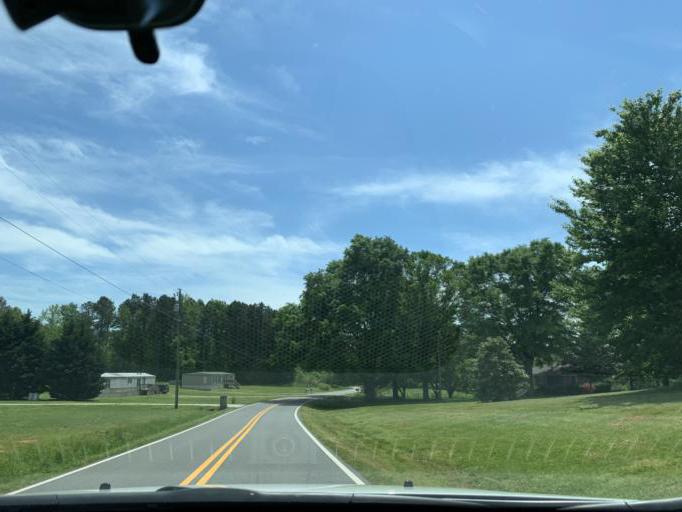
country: US
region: Georgia
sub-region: Hall County
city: Flowery Branch
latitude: 34.2765
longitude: -84.0242
